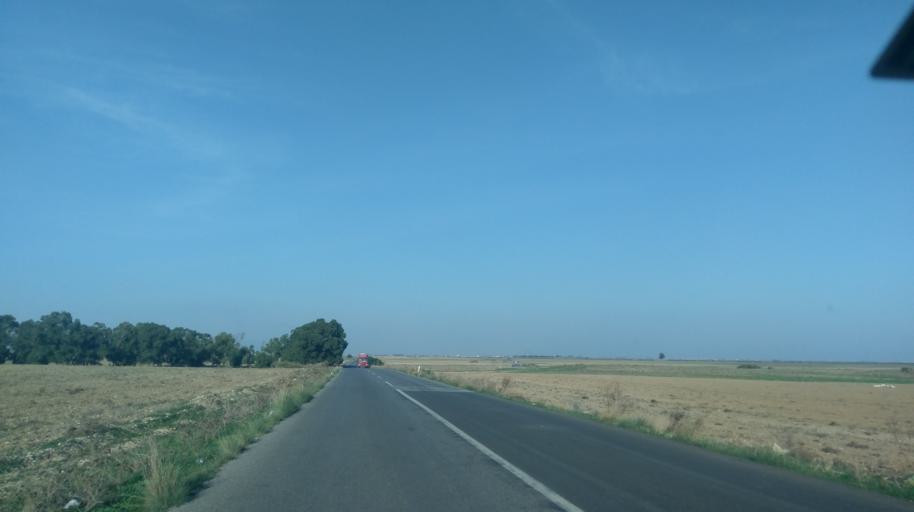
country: CY
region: Ammochostos
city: Achna
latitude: 35.1302
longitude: 33.7371
